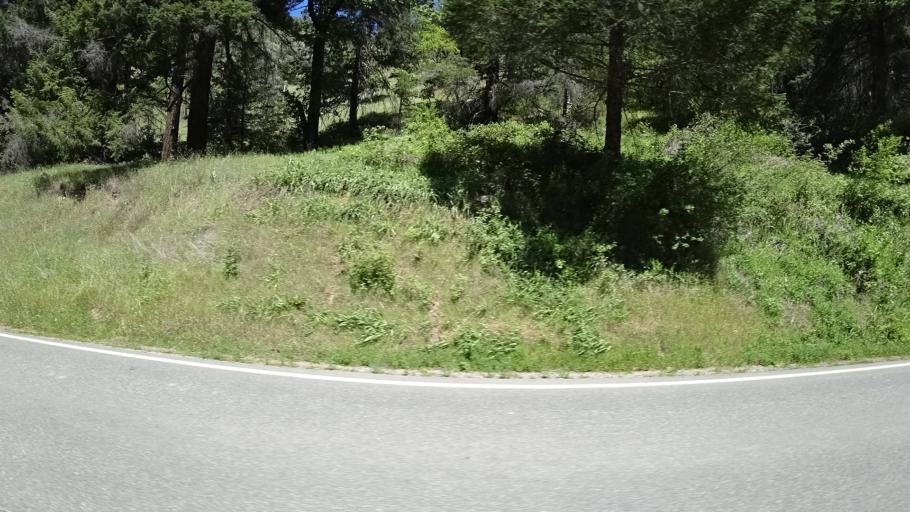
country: US
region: California
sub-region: Trinity County
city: Hayfork
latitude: 40.7489
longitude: -123.2739
